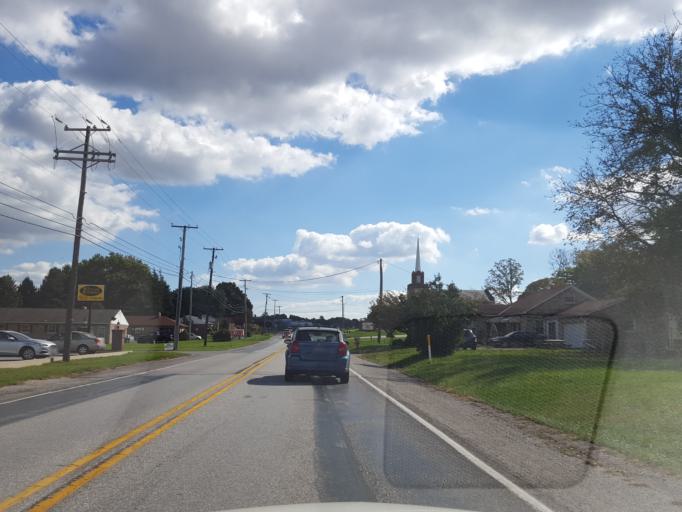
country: US
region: Pennsylvania
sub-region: York County
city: Yoe
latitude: 39.9244
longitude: -76.6353
